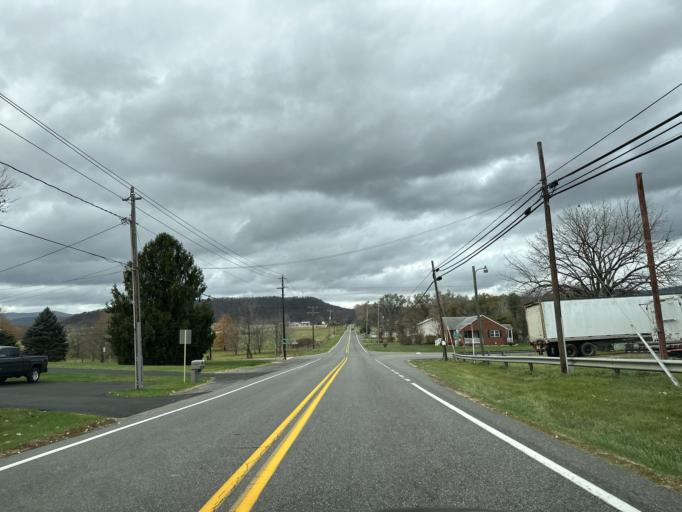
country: US
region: Virginia
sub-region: Rockingham County
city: Dayton
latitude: 38.4790
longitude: -78.9966
